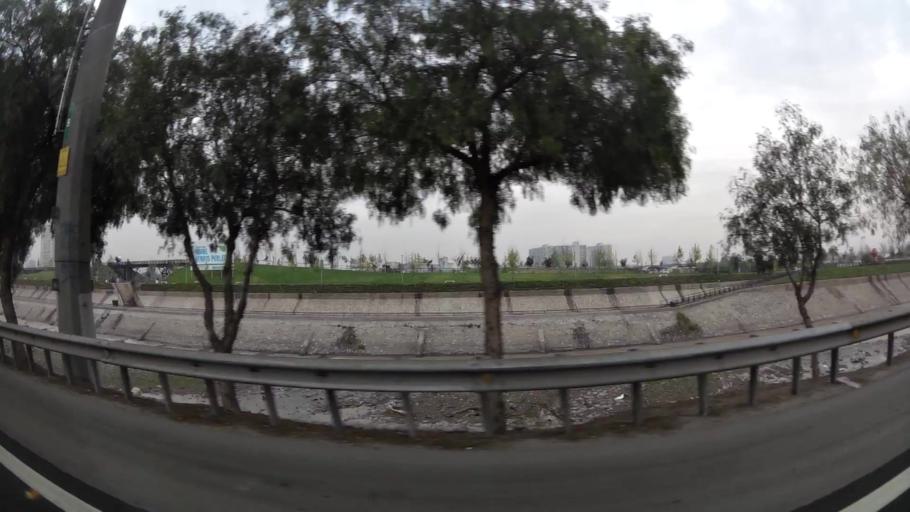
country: CL
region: Santiago Metropolitan
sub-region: Provincia de Santiago
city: Santiago
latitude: -33.4225
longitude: -70.6808
